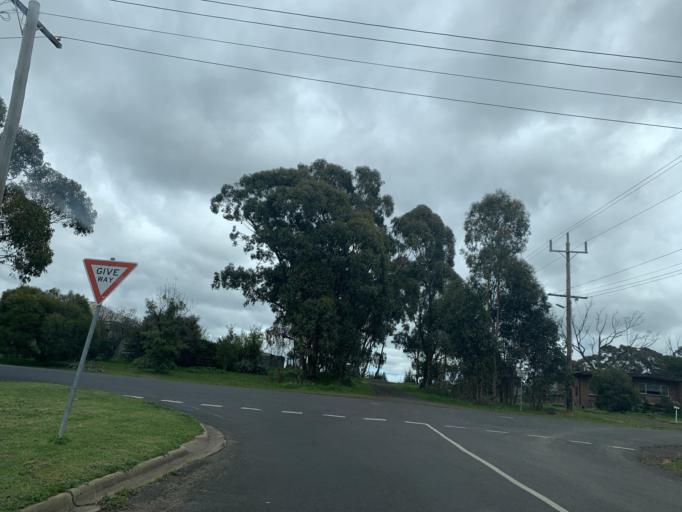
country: AU
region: Victoria
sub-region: Whittlesea
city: Whittlesea
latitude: -37.2100
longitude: 145.0402
